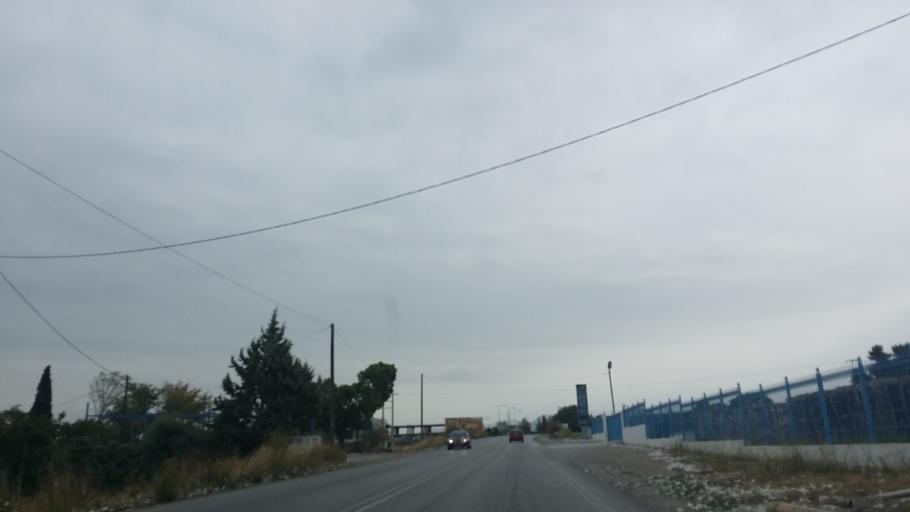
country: GR
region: Central Greece
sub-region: Nomos Voiotias
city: Thivai
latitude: 38.3273
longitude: 23.2864
